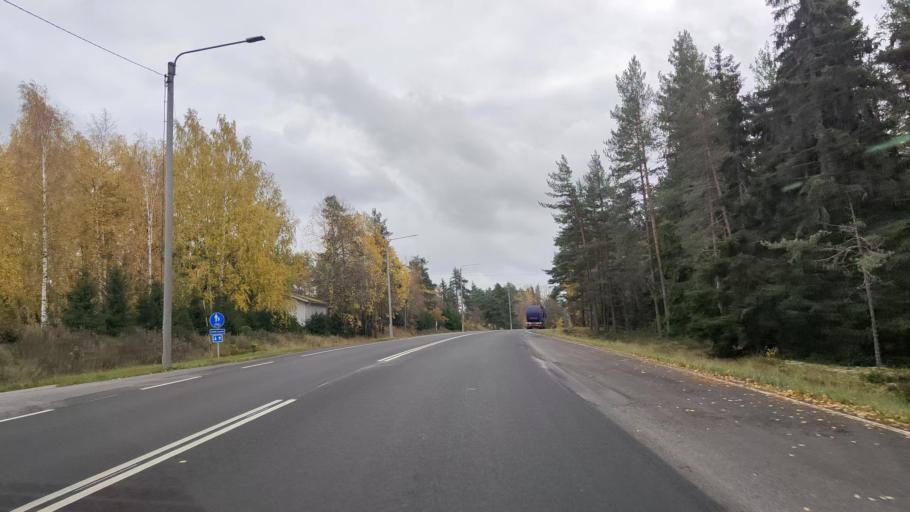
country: FI
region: Varsinais-Suomi
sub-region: Turku
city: Kaarina
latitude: 60.4519
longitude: 22.3716
